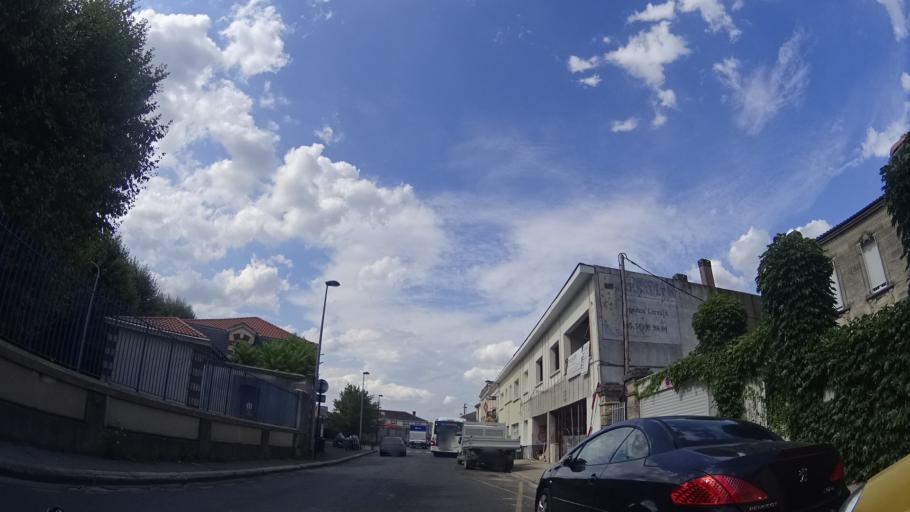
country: FR
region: Aquitaine
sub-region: Departement de la Gironde
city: Begles
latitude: 44.8183
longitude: -0.5662
